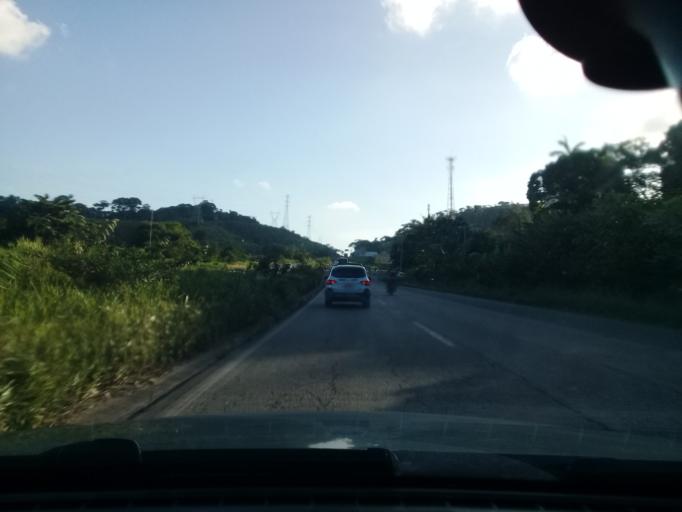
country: BR
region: Pernambuco
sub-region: Jaboatao Dos Guararapes
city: Jaboatao dos Guararapes
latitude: -8.0811
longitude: -34.9939
